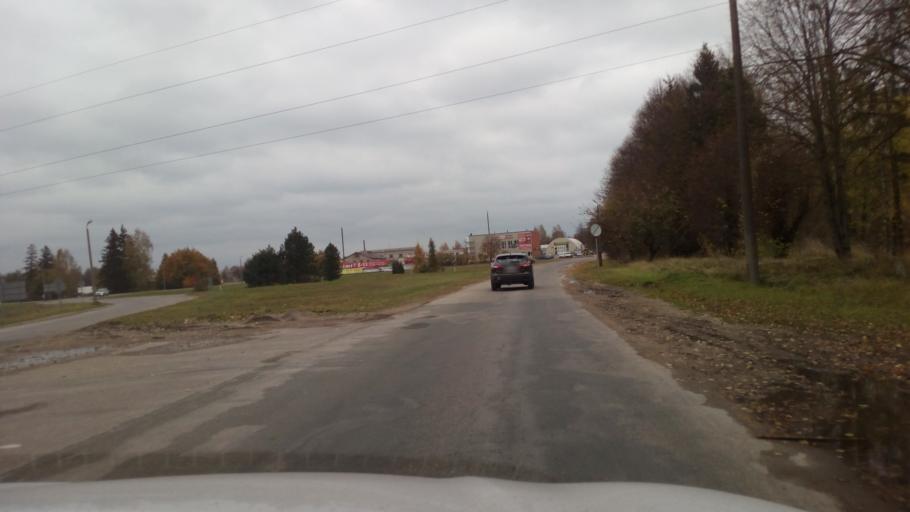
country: LV
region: Talsu Rajons
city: Talsi
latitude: 57.2317
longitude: 22.5857
